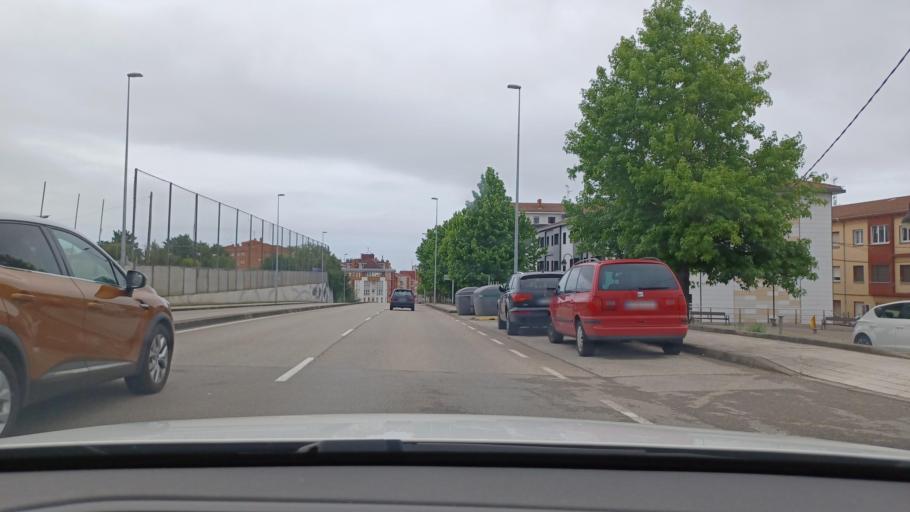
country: ES
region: Asturias
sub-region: Province of Asturias
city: Gijon
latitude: 43.5285
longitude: -5.6549
